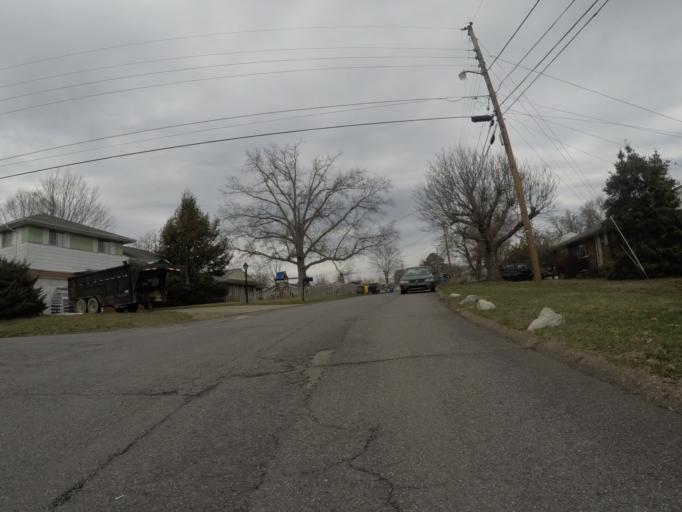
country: US
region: West Virginia
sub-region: Cabell County
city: Pea Ridge
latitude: 38.3925
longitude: -82.3779
